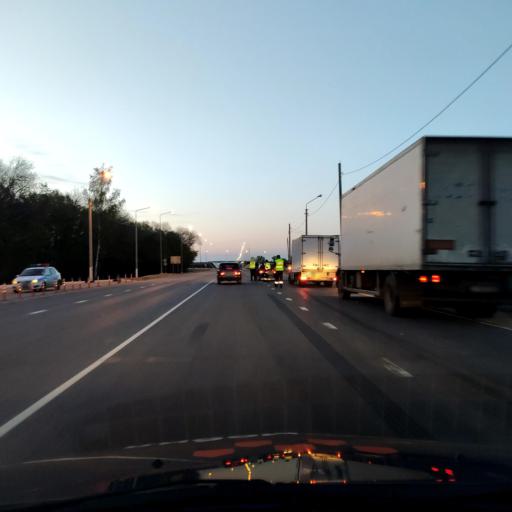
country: RU
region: Orjol
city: Zmiyevka
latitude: 52.7042
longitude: 36.3675
